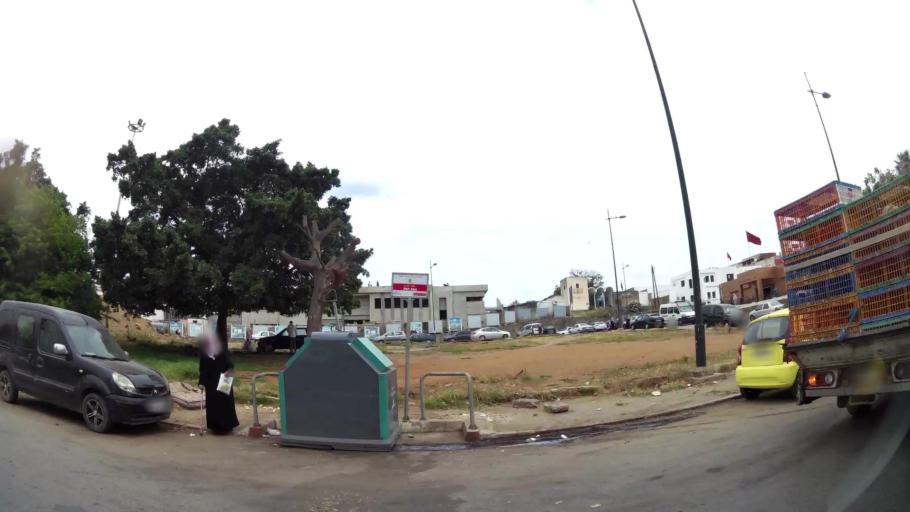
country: MA
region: Rabat-Sale-Zemmour-Zaer
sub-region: Rabat
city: Rabat
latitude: 33.9957
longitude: -6.8712
